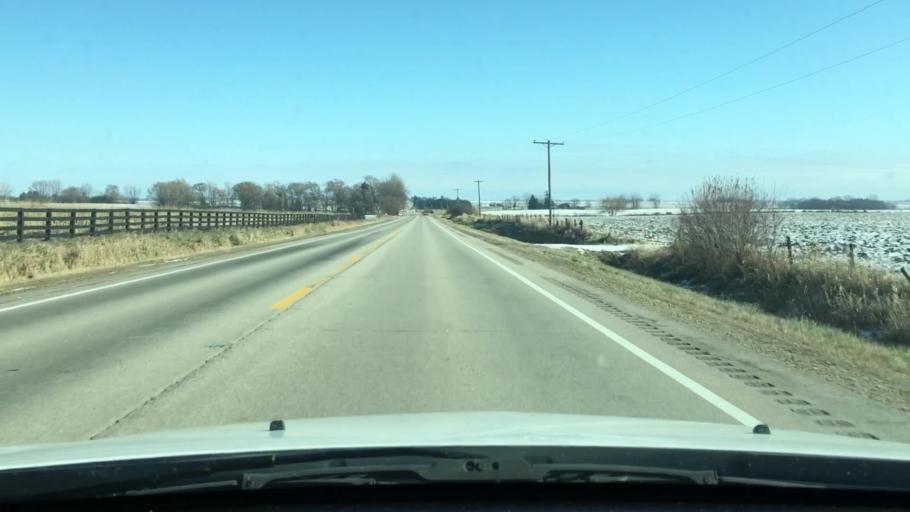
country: US
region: Illinois
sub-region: DeKalb County
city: Malta
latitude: 42.0009
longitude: -88.8710
